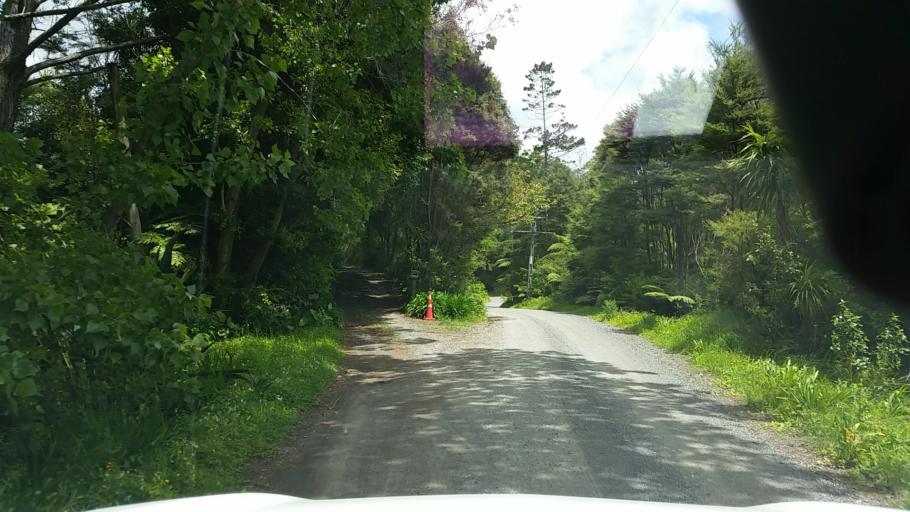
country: NZ
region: Auckland
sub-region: Auckland
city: Rosebank
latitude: -36.8533
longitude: 174.5874
